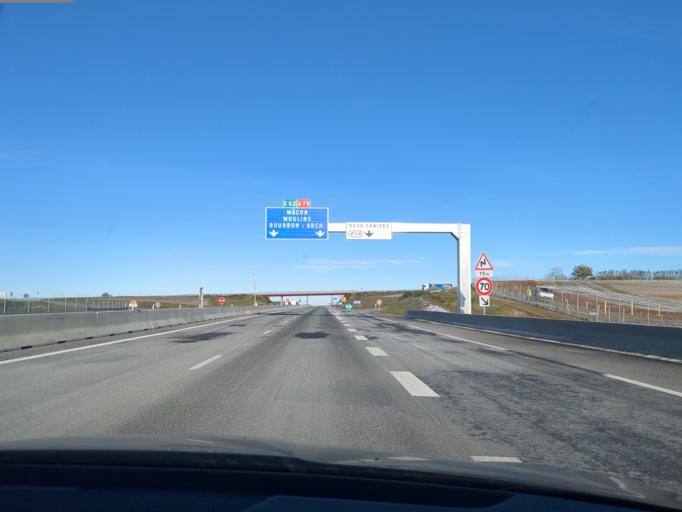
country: FR
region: Auvergne
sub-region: Departement de l'Allier
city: Montmarault
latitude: 46.3734
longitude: 3.0286
